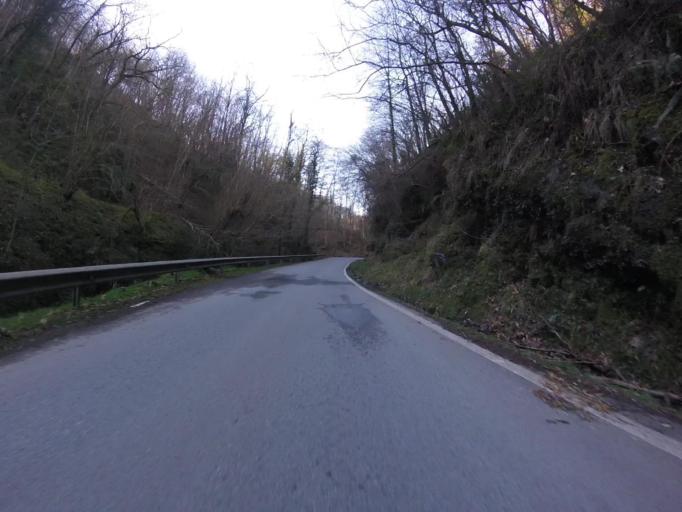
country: ES
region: Navarre
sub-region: Provincia de Navarra
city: Lesaka
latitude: 43.2516
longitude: -1.7216
